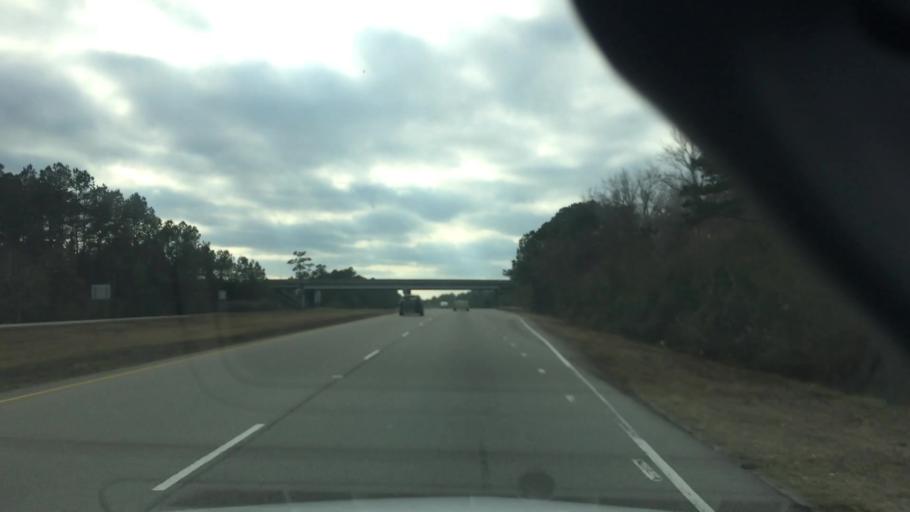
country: US
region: North Carolina
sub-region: Brunswick County
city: Shallotte
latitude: 33.9778
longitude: -78.4032
